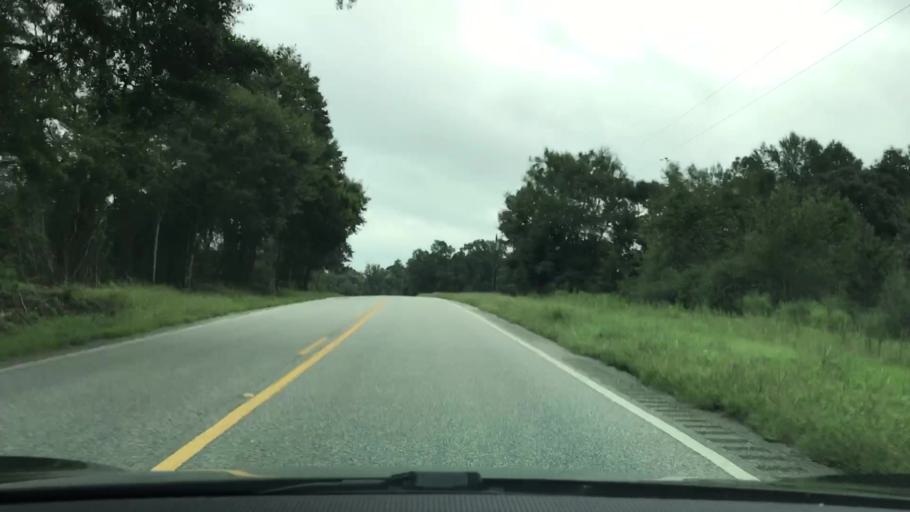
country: US
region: Alabama
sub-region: Geneva County
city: Samson
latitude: 31.0260
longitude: -86.1157
